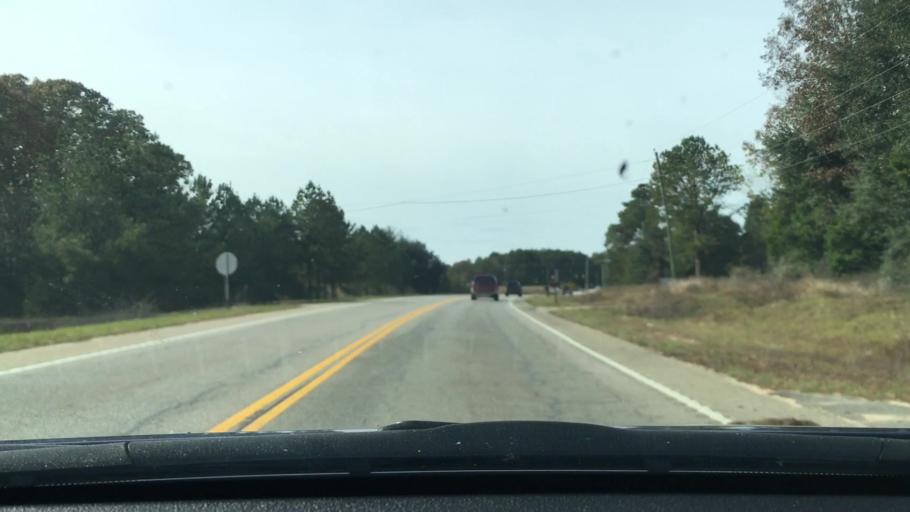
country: US
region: South Carolina
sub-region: Sumter County
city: Cherryvale
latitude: 33.9378
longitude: -80.4713
